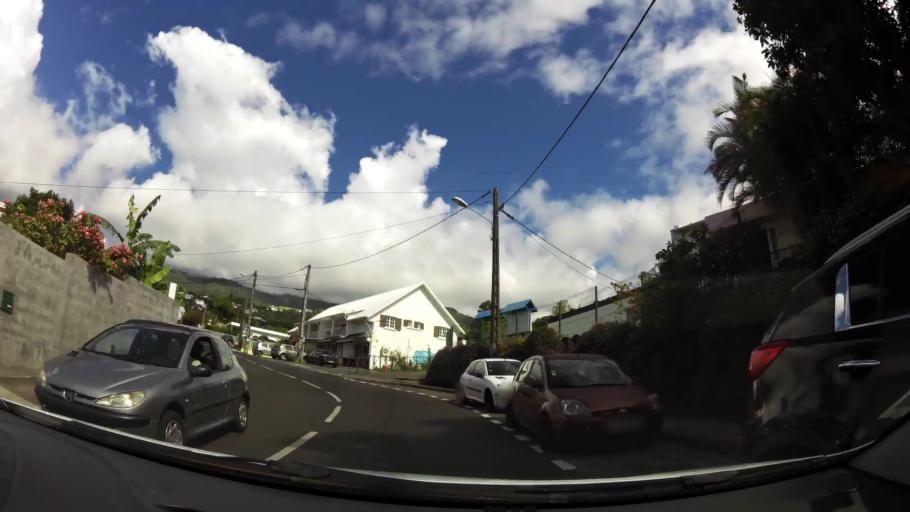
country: RE
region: Reunion
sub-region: Reunion
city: Saint-Denis
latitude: -20.9261
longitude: 55.4936
